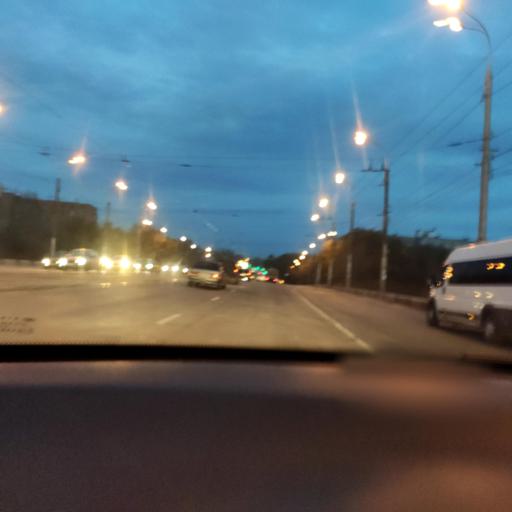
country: RU
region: Samara
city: Samara
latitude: 53.2134
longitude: 50.2703
